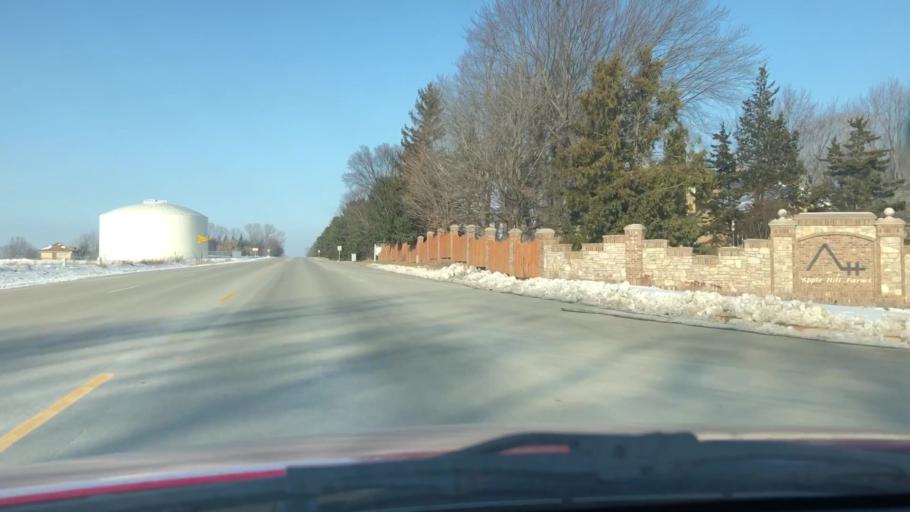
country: US
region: Wisconsin
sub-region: Outagamie County
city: Kimberly
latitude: 44.3334
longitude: -88.3750
